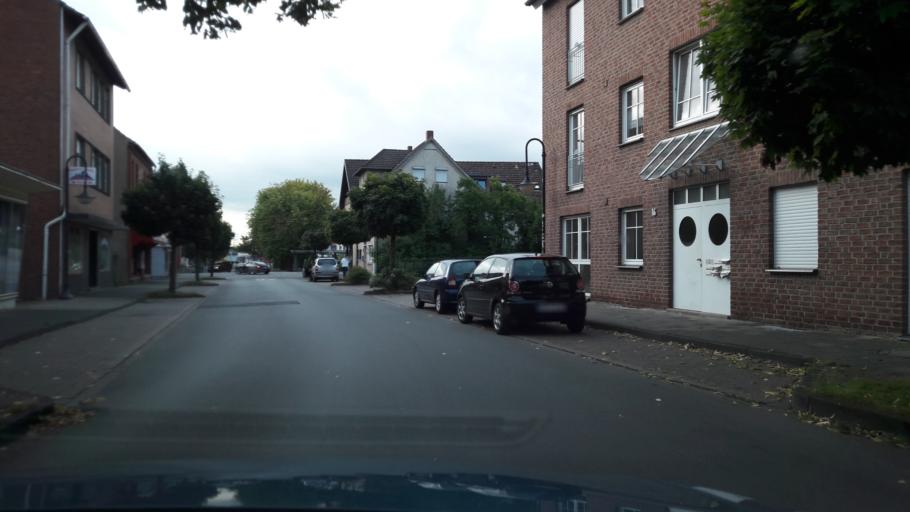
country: DE
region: North Rhine-Westphalia
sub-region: Regierungsbezirk Munster
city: Ennigerloh
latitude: 51.8361
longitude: 8.0266
